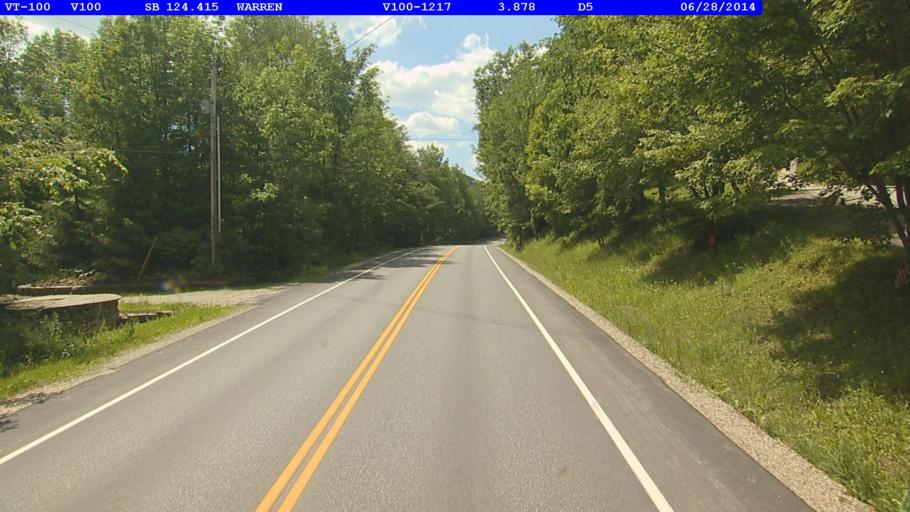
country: US
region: Vermont
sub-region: Washington County
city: Northfield
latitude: 44.1141
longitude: -72.8578
